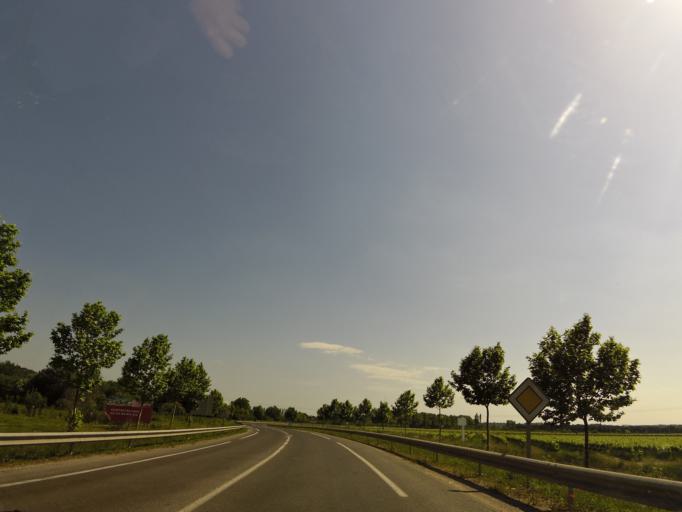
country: FR
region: Languedoc-Roussillon
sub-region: Departement du Gard
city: Sommieres
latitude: 43.7778
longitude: 4.0864
